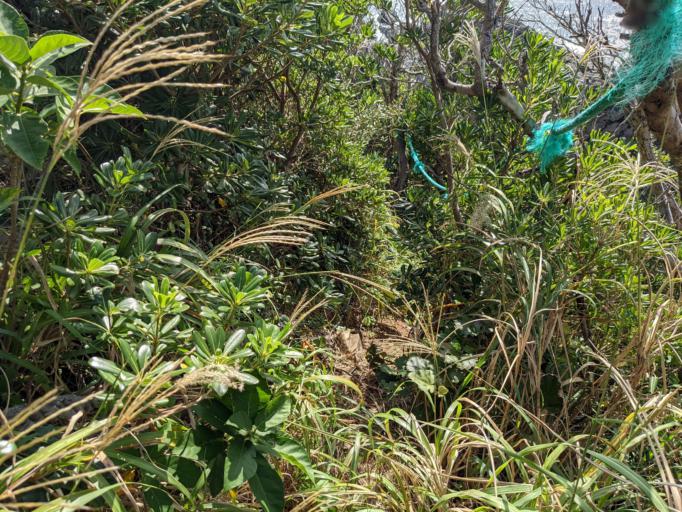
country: JP
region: Wakayama
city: Shingu
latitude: 33.4358
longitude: 135.7596
